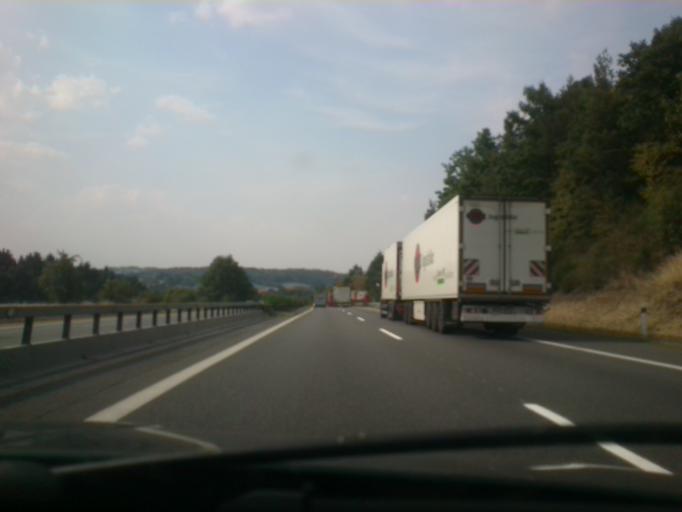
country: CZ
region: Central Bohemia
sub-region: Okres Praha-Vychod
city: Mnichovice
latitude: 49.9046
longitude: 14.7353
